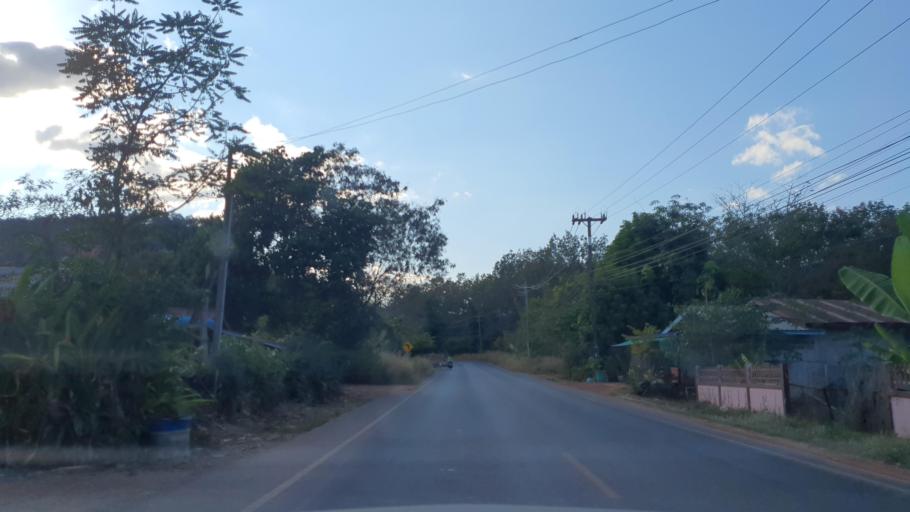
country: TH
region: Changwat Bueng Kan
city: Si Wilai
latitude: 18.1401
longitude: 103.8910
